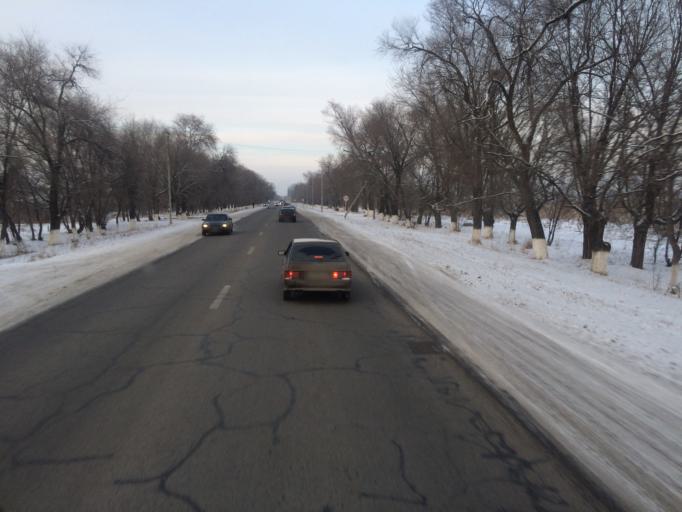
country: KZ
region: Almaty Oblysy
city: Burunday
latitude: 43.2616
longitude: 76.6695
